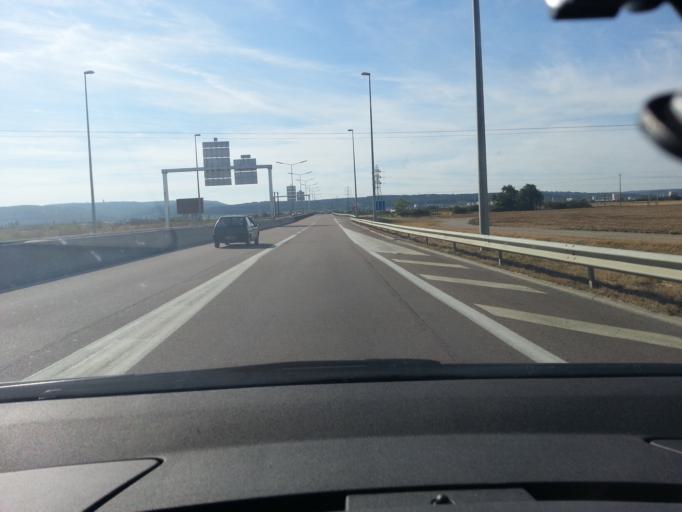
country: FR
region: Bourgogne
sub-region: Departement de la Cote-d'Or
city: Longvic
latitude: 47.2751
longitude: 5.0371
